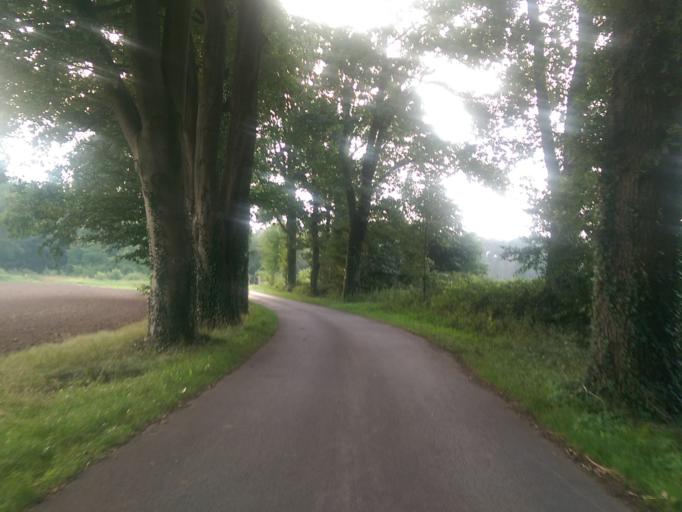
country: DE
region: North Rhine-Westphalia
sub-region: Regierungsbezirk Detmold
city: Rheda-Wiedenbruck
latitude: 51.8714
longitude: 8.3442
